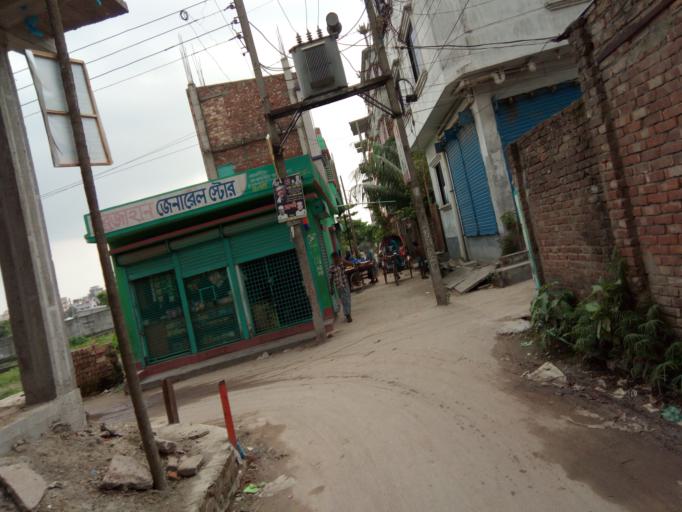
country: BD
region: Dhaka
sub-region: Dhaka
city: Dhaka
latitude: 23.7025
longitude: 90.4840
